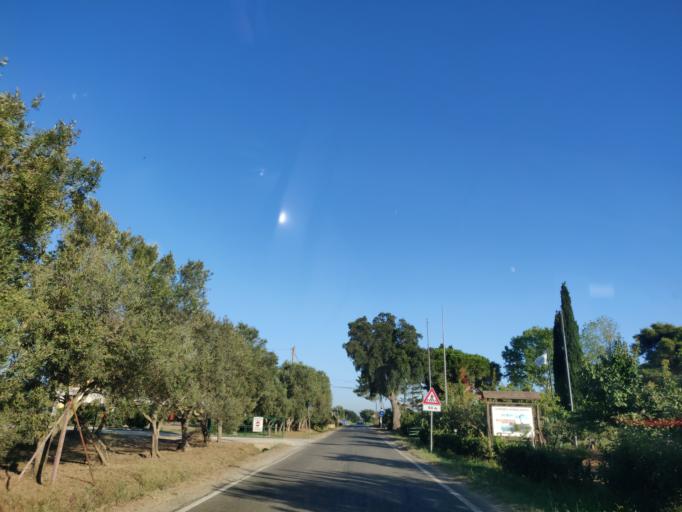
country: IT
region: Latium
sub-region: Provincia di Viterbo
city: Montalto di Castro
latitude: 42.2960
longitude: 11.6495
